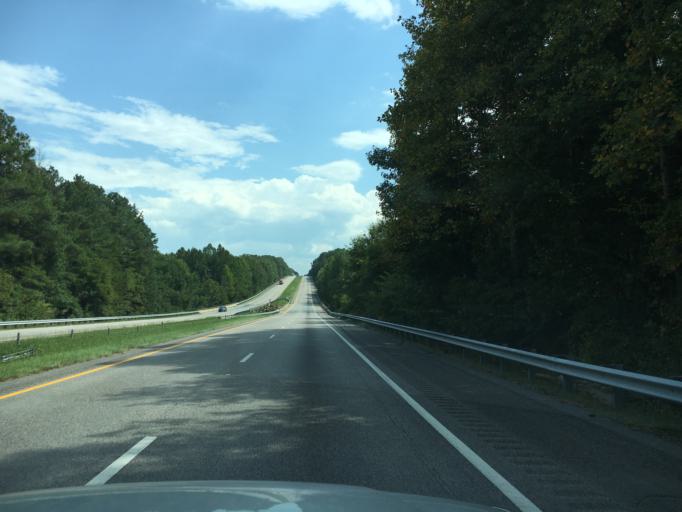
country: US
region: South Carolina
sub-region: Laurens County
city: Clinton
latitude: 34.5492
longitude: -81.8877
